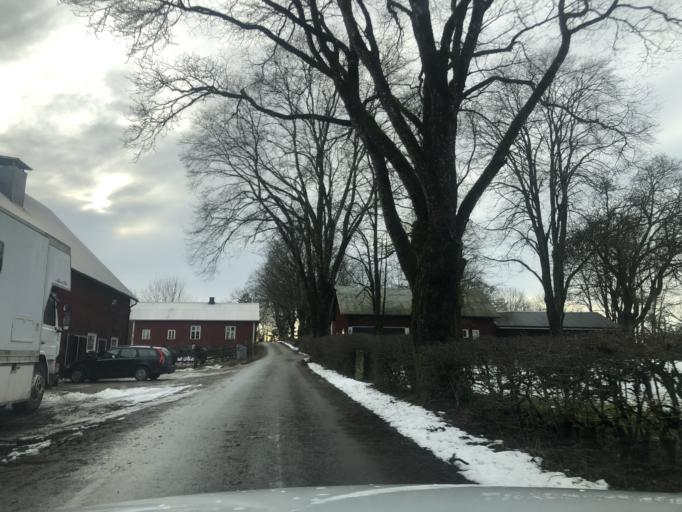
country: SE
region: Vaestra Goetaland
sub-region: Ulricehamns Kommun
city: Ulricehamn
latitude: 57.8066
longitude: 13.5100
